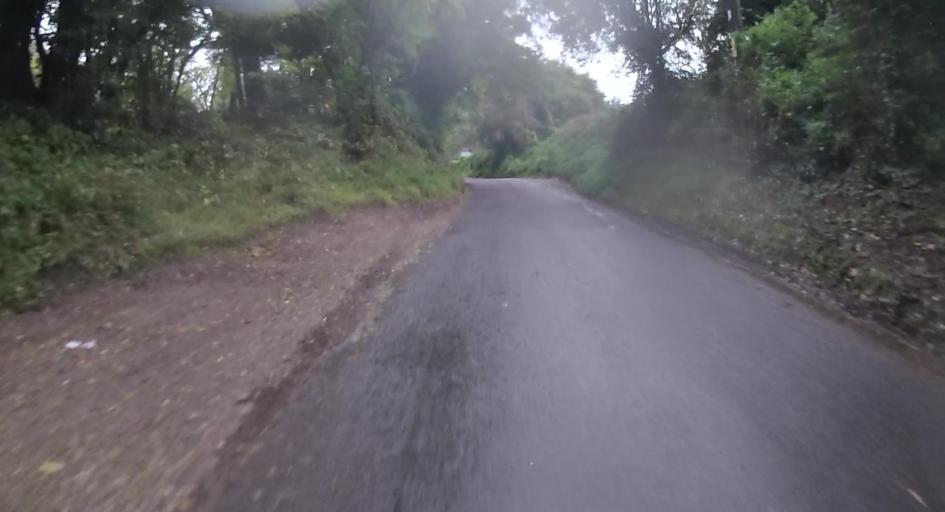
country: GB
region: England
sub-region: West Berkshire
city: Thatcham
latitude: 51.3985
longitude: -1.2078
